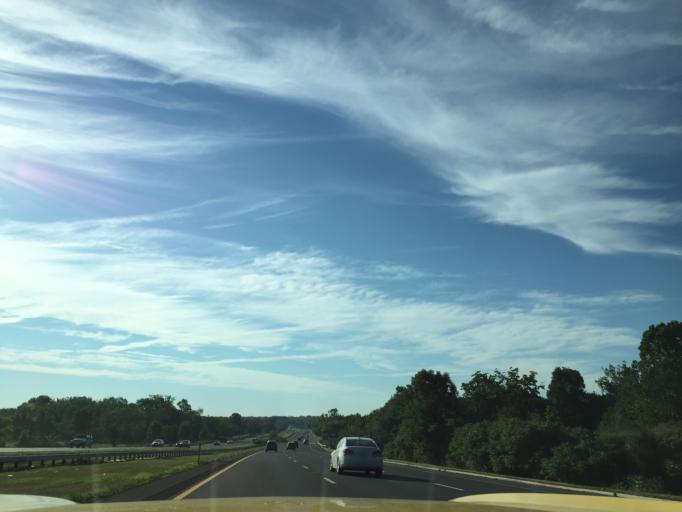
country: US
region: New Jersey
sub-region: Hunterdon County
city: Hampton
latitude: 40.6421
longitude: -74.9919
